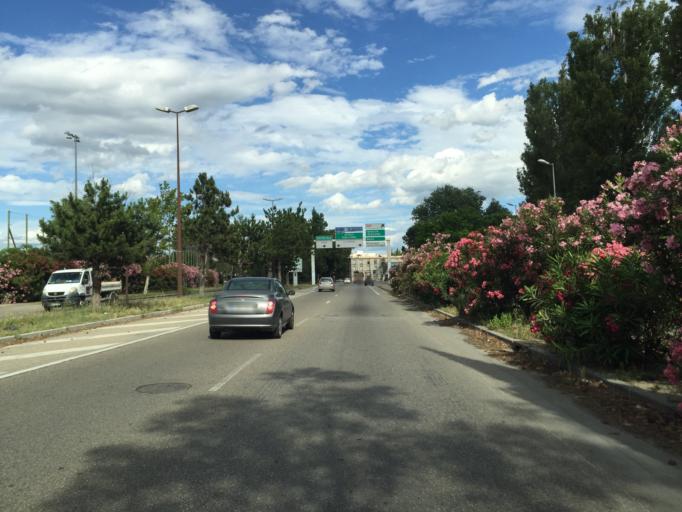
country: FR
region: Provence-Alpes-Cote d'Azur
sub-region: Departement du Vaucluse
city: Avignon
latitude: 43.9286
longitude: 4.8068
